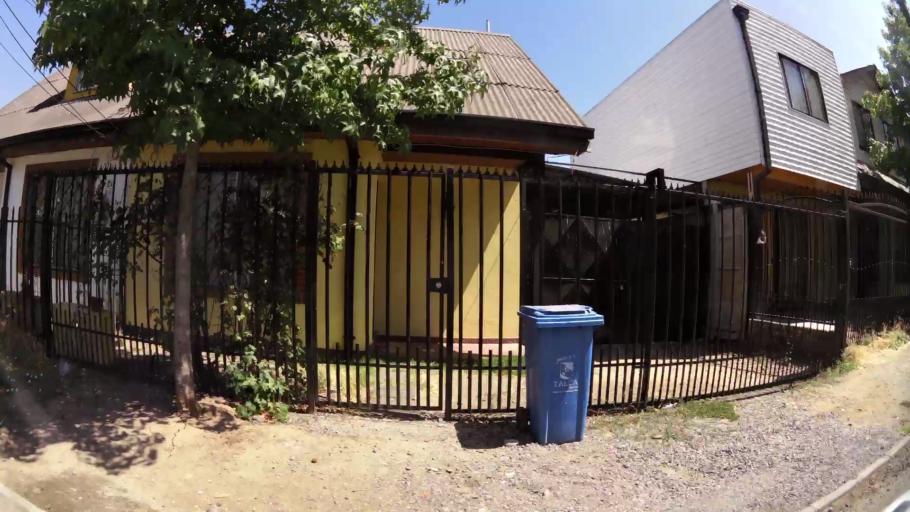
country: CL
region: Maule
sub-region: Provincia de Talca
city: Talca
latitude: -35.4277
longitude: -71.6281
